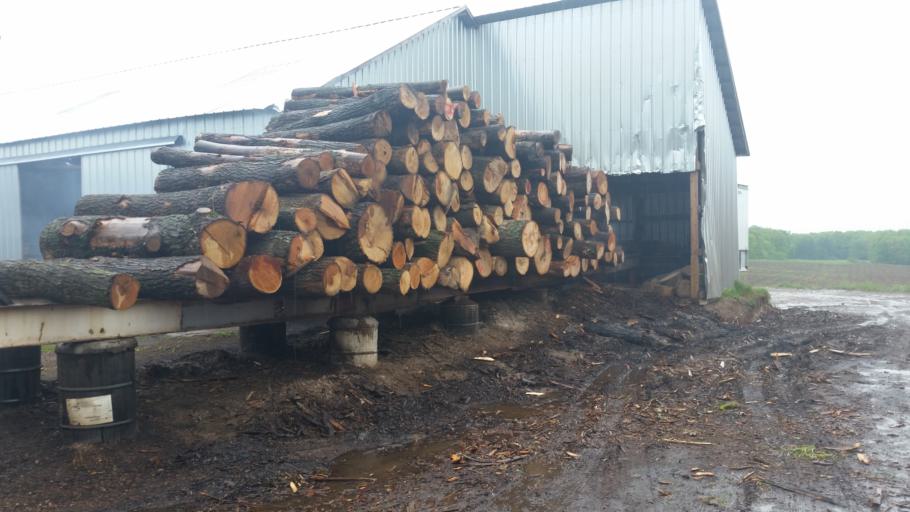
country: US
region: Wisconsin
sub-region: Clark County
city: Loyal
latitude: 44.6477
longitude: -90.4575
